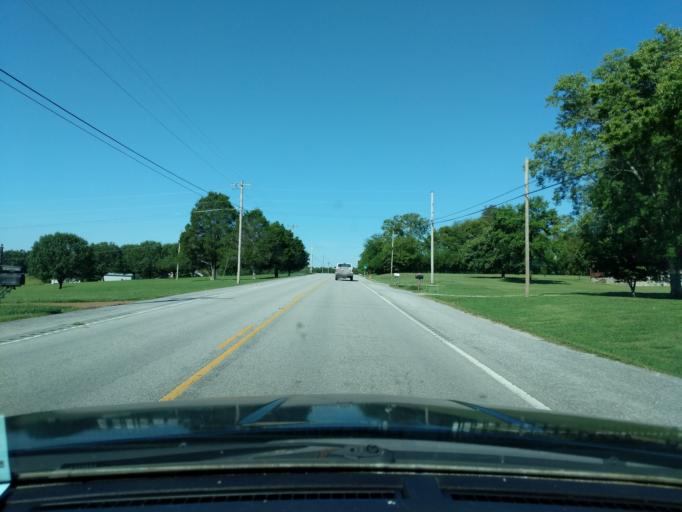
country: US
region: Tennessee
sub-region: Smith County
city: Carthage
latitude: 36.2592
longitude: -86.0843
